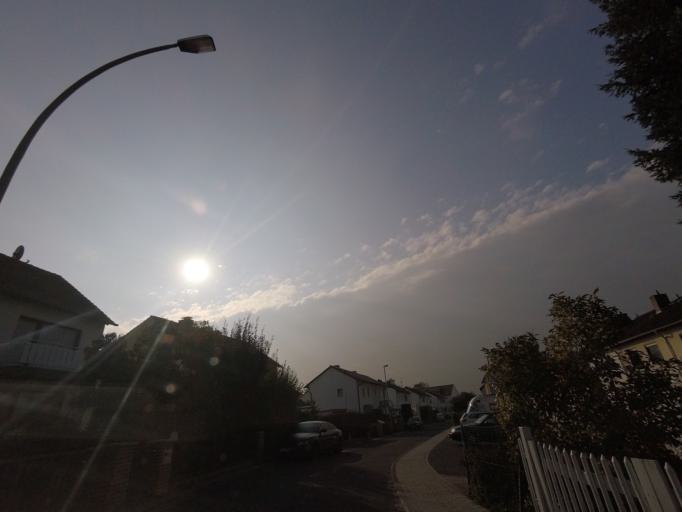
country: DE
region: Hesse
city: Schwalbach am Taunus
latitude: 50.1465
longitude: 8.5415
